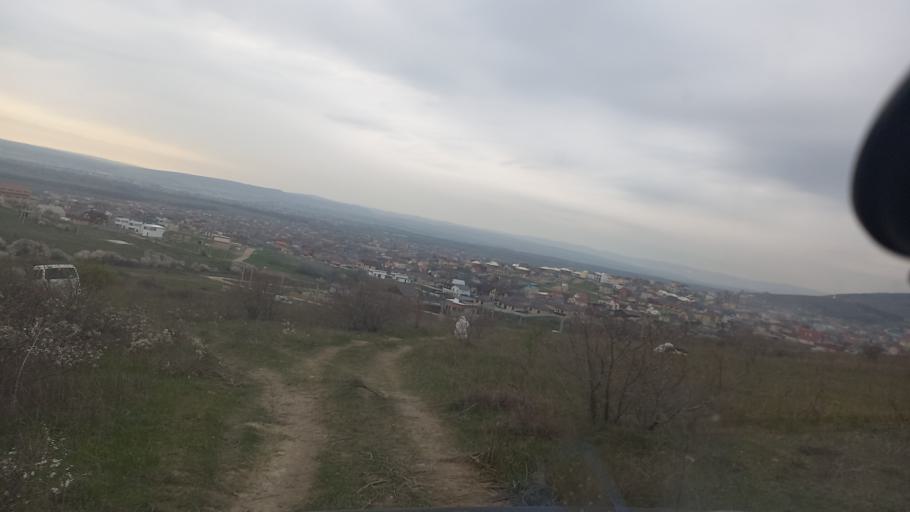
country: RU
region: Krasnodarskiy
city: Anapa
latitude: 44.8517
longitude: 37.3431
